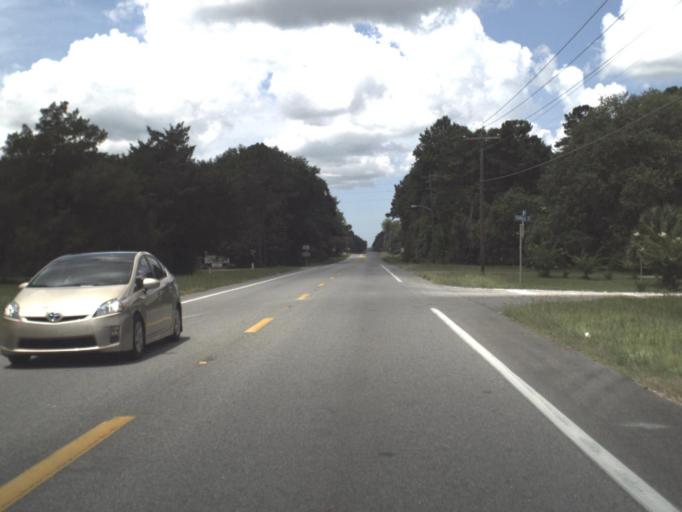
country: US
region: Florida
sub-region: Taylor County
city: Perry
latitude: 30.1068
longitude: -83.6031
